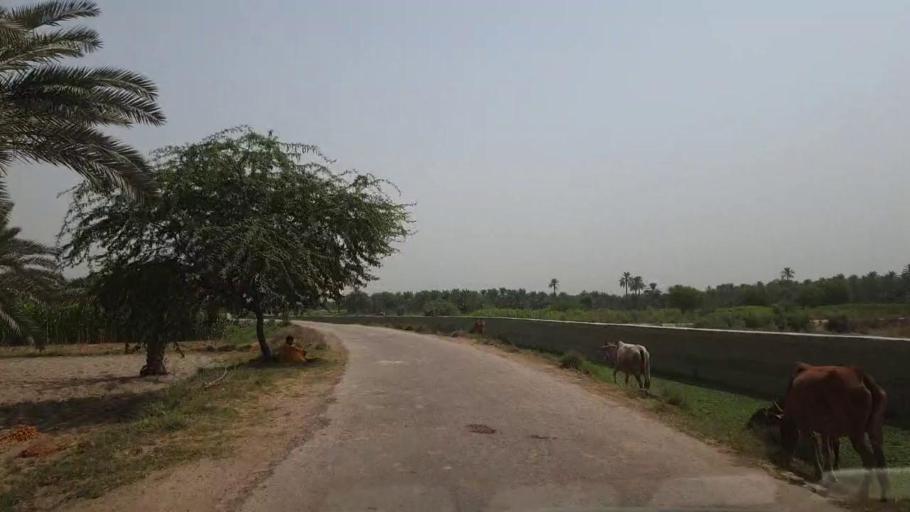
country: PK
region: Sindh
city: Gambat
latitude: 27.4256
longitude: 68.5596
